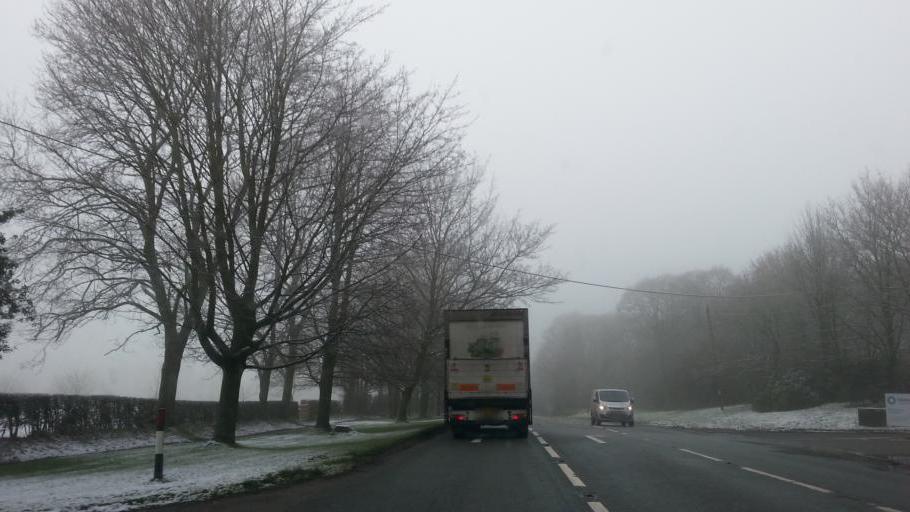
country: GB
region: England
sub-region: Cheshire East
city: Eaton
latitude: 53.1845
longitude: -2.2123
